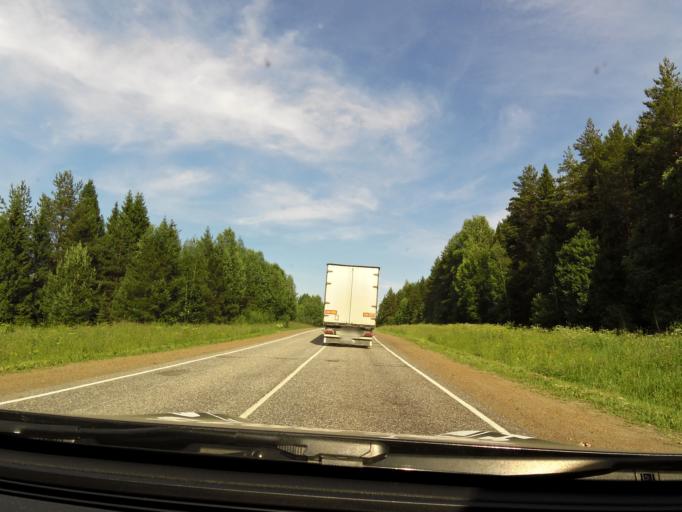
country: RU
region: Kirov
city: Belaya Kholunitsa
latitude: 58.8075
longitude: 50.5591
